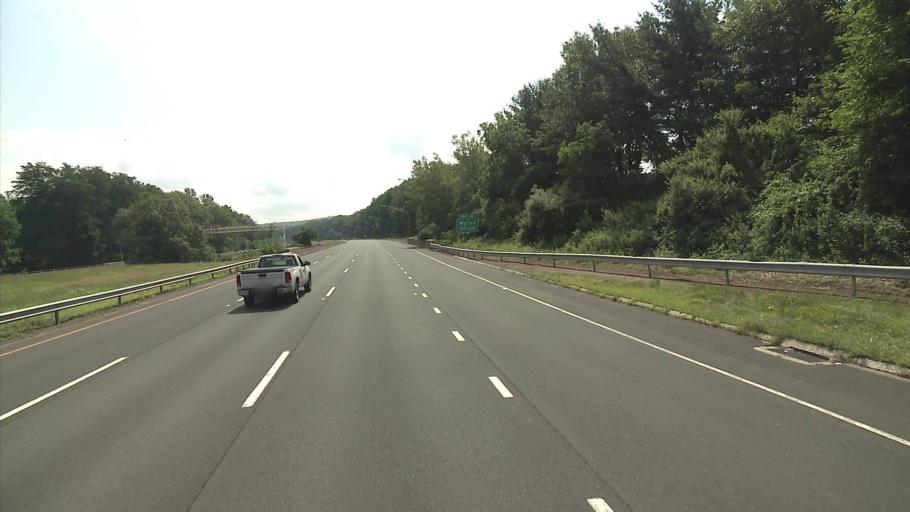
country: US
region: Connecticut
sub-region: Hartford County
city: Manchester
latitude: 41.7616
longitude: -72.5145
